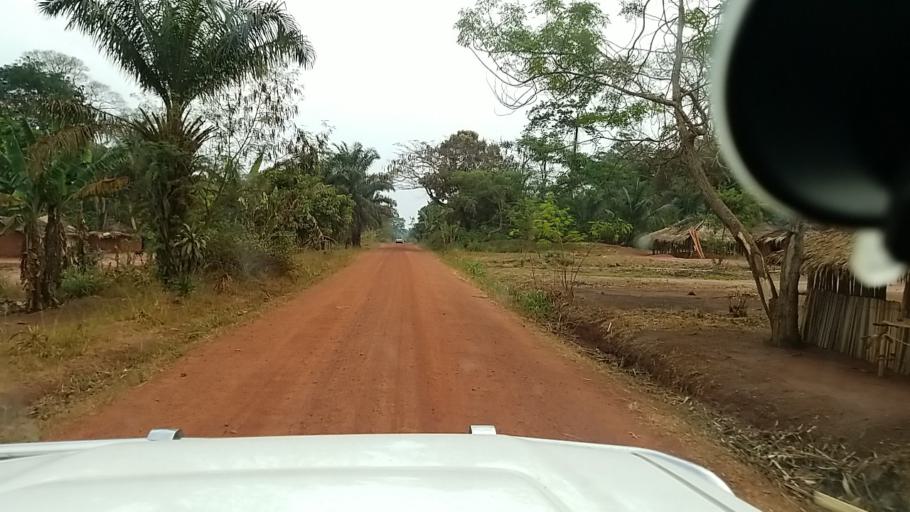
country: CD
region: Equateur
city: Gemena
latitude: 2.9665
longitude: 19.9003
